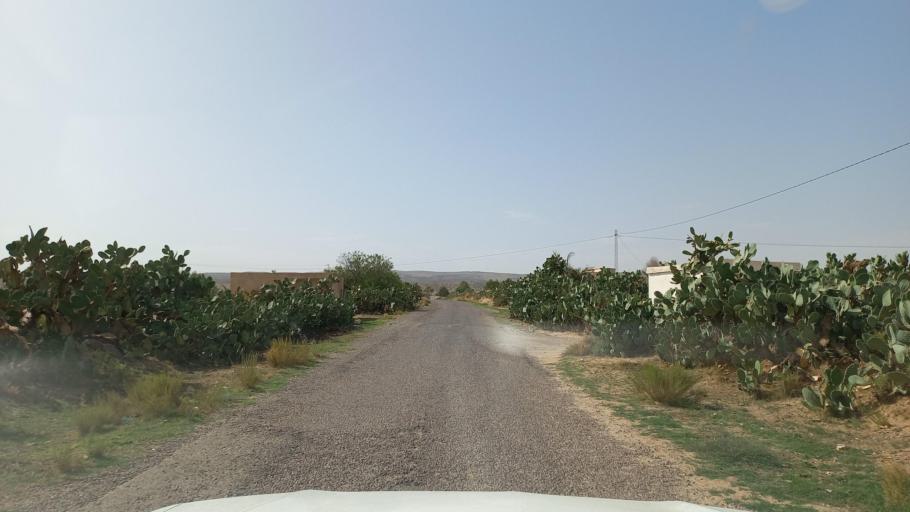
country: TN
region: Al Qasrayn
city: Kasserine
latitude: 35.2998
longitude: 8.9531
